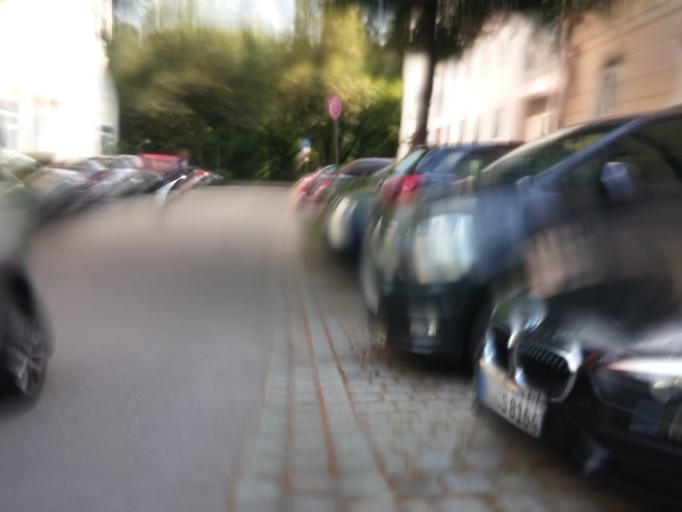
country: DE
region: Bavaria
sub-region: Upper Bavaria
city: Munich
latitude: 48.1556
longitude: 11.5702
